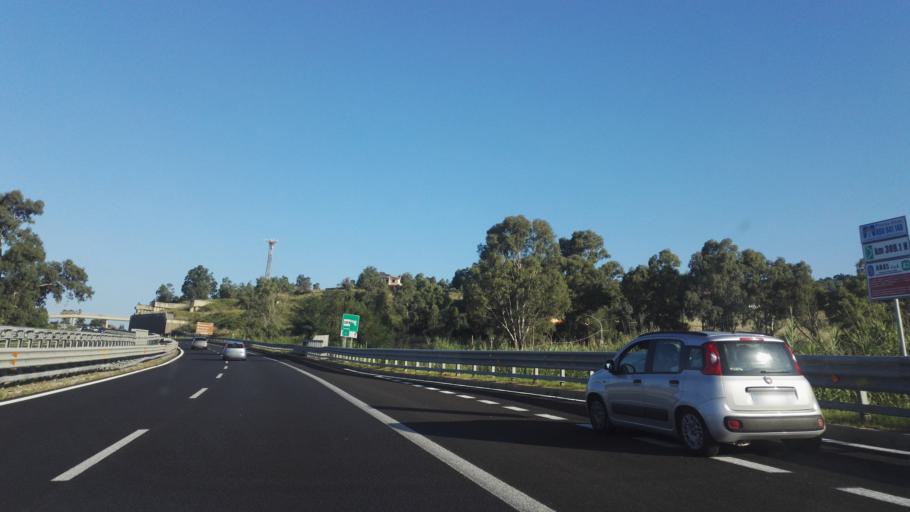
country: IT
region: Calabria
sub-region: Provincia di Catanzaro
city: Falerna Scalo
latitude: 38.9740
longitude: 16.1514
